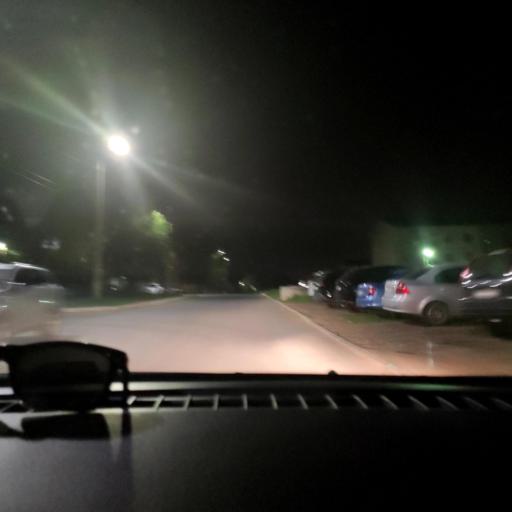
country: RU
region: Samara
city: Novokuybyshevsk
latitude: 53.1027
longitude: 49.9736
